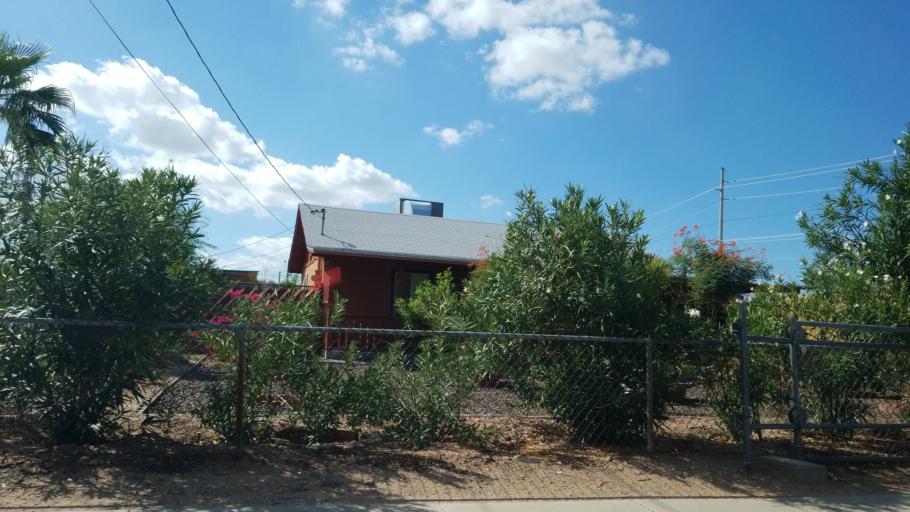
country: US
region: Arizona
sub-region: Maricopa County
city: Glendale
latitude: 33.5839
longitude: -112.0970
